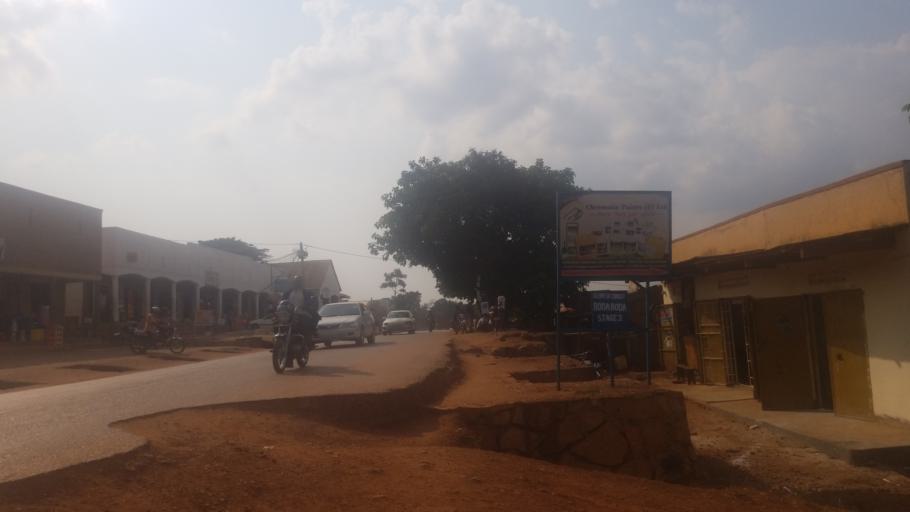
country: UG
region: Central Region
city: Kampala Central Division
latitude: 0.3377
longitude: 32.5553
